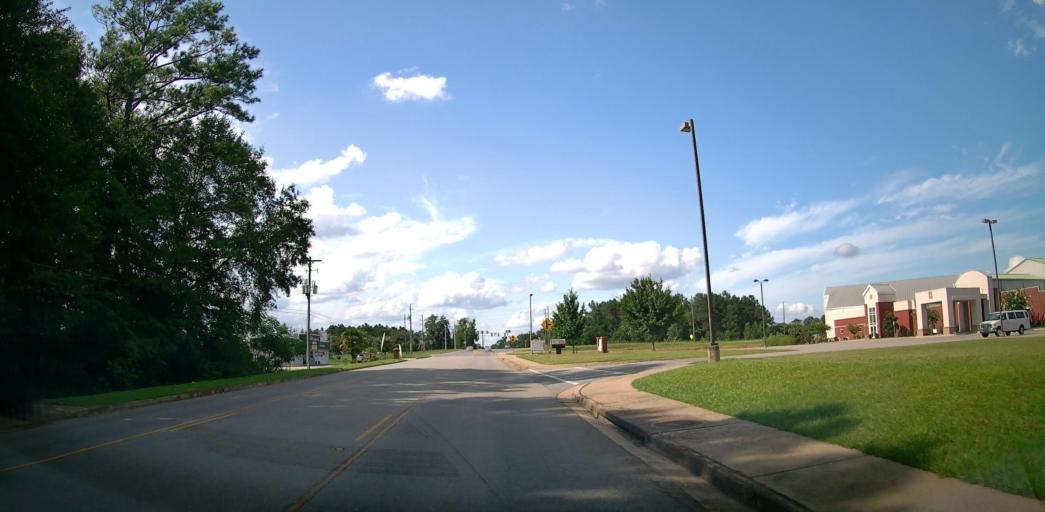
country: US
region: Georgia
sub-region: Houston County
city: Robins Air Force Base
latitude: 32.5483
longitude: -83.6045
